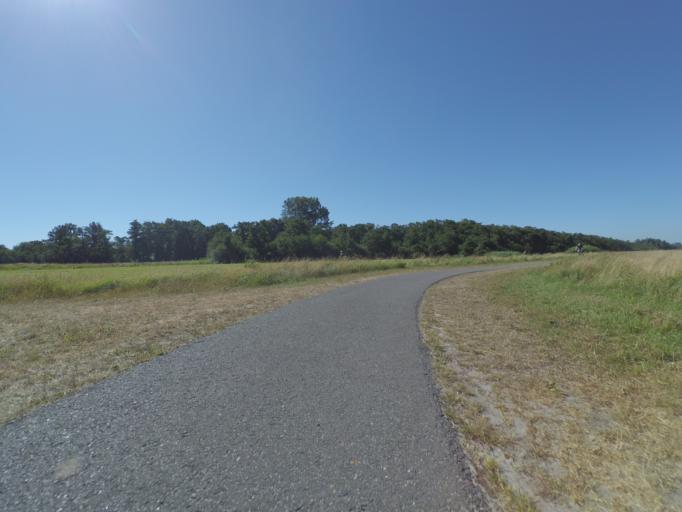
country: NL
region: Utrecht
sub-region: Gemeente Utrecht
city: Utrecht
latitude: 52.1323
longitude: 5.1274
